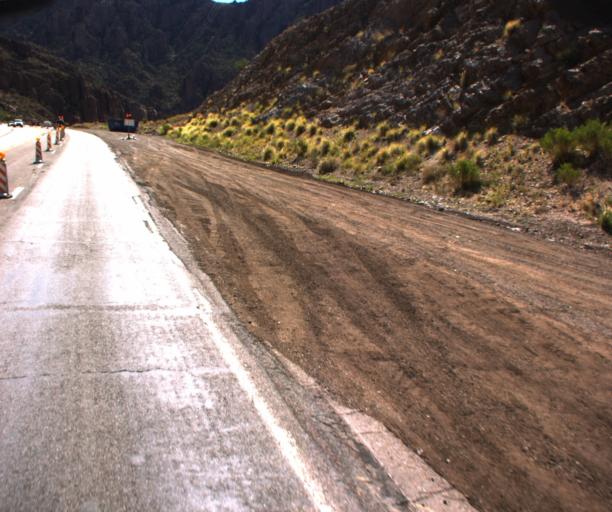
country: US
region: Arizona
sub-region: Pinal County
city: Superior
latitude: 33.3037
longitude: -111.0875
